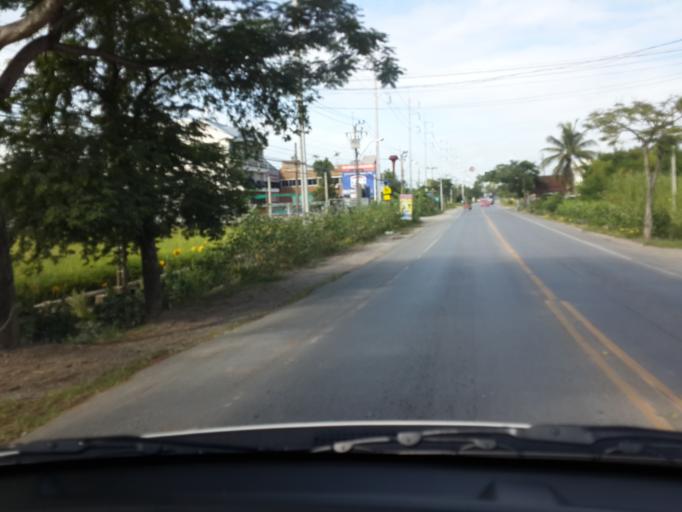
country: TH
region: Bangkok
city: Khlong Sam Wa
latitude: 13.8486
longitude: 100.7946
